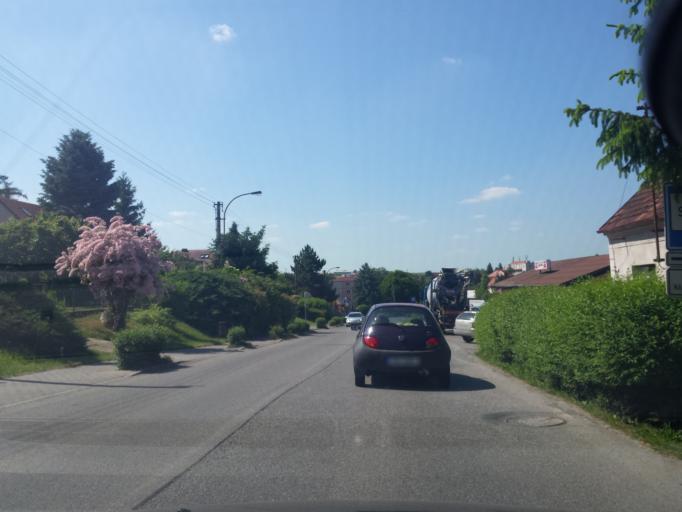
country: CZ
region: Central Bohemia
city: Velke Prilepy
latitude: 50.1584
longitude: 14.3145
